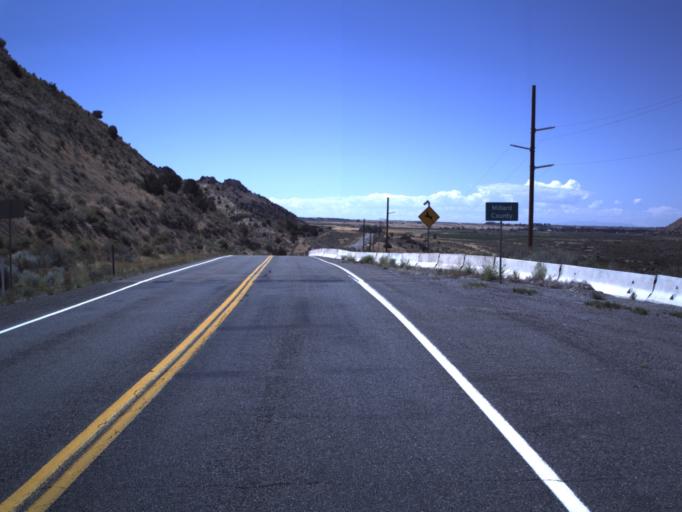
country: US
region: Utah
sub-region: Juab County
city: Nephi
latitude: 39.5543
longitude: -112.2173
